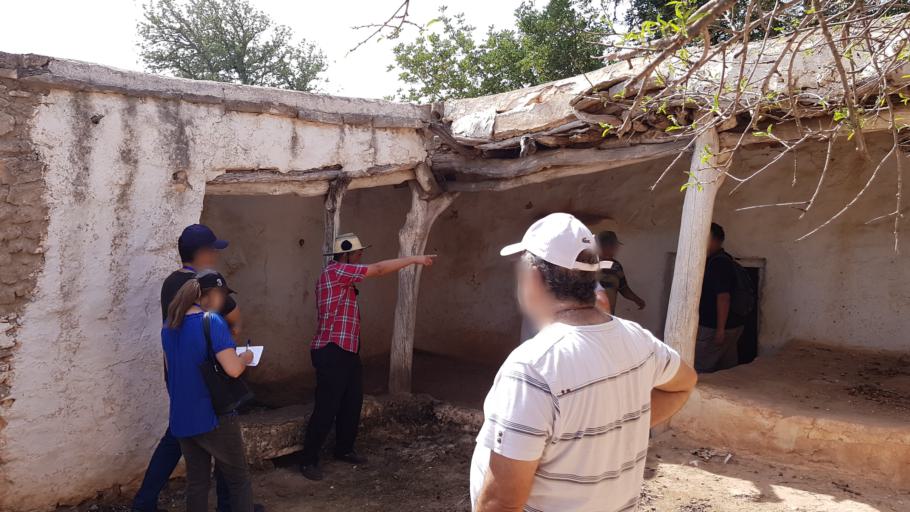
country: MA
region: Taza-Al Hoceima-Taounate
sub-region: Al-Hoceima
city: Rouadi
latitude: 35.1745
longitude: -4.1722
